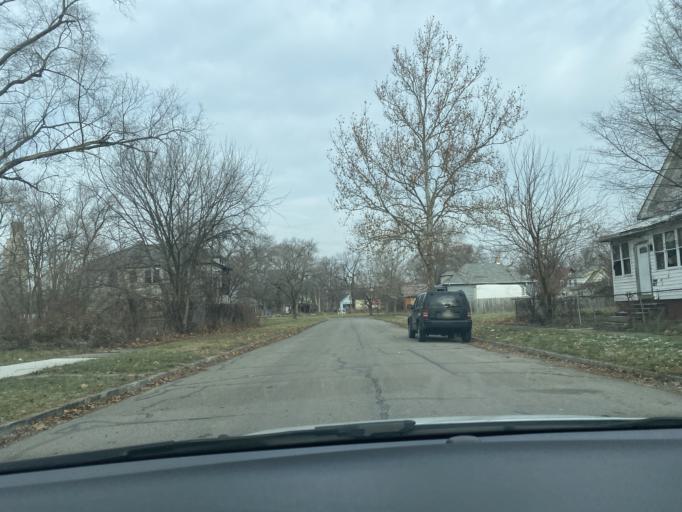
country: US
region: Michigan
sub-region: Wayne County
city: Highland Park
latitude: 42.3705
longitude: -83.1377
